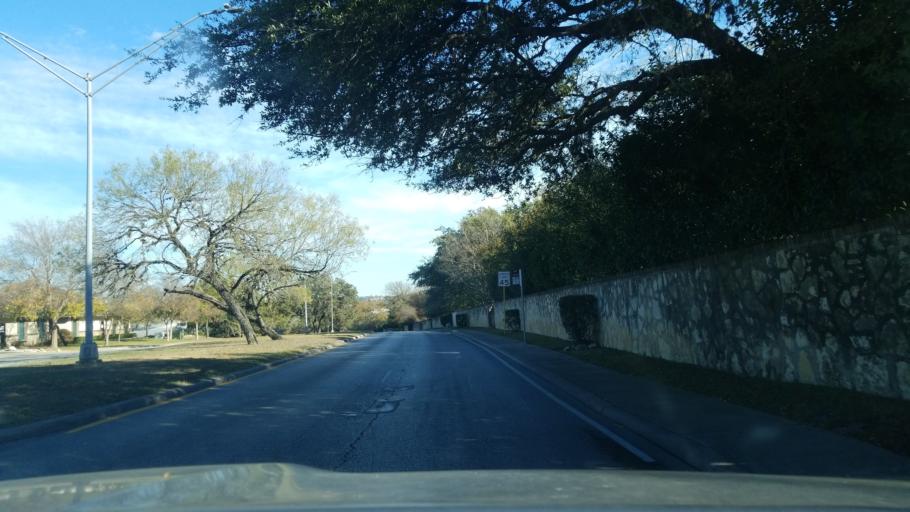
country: US
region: Texas
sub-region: Bexar County
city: Shavano Park
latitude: 29.6001
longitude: -98.5230
